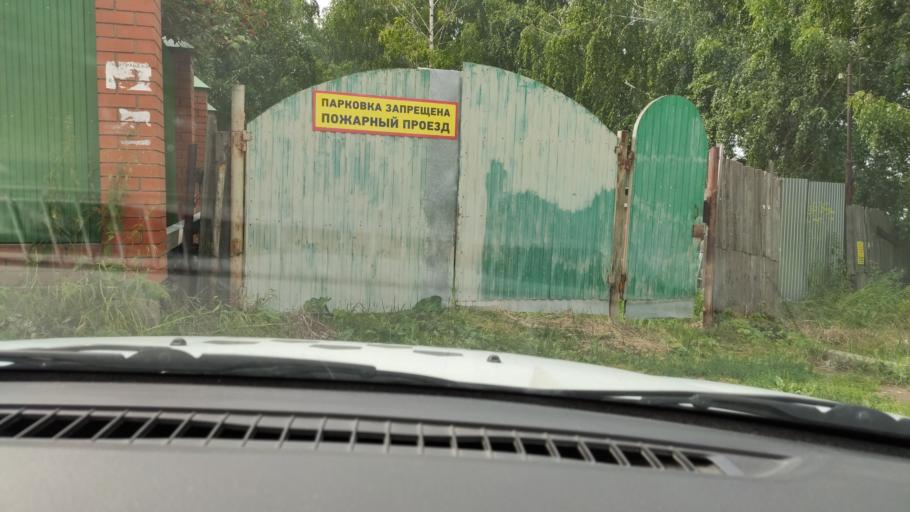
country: RU
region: Perm
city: Sylva
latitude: 58.0486
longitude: 56.7345
